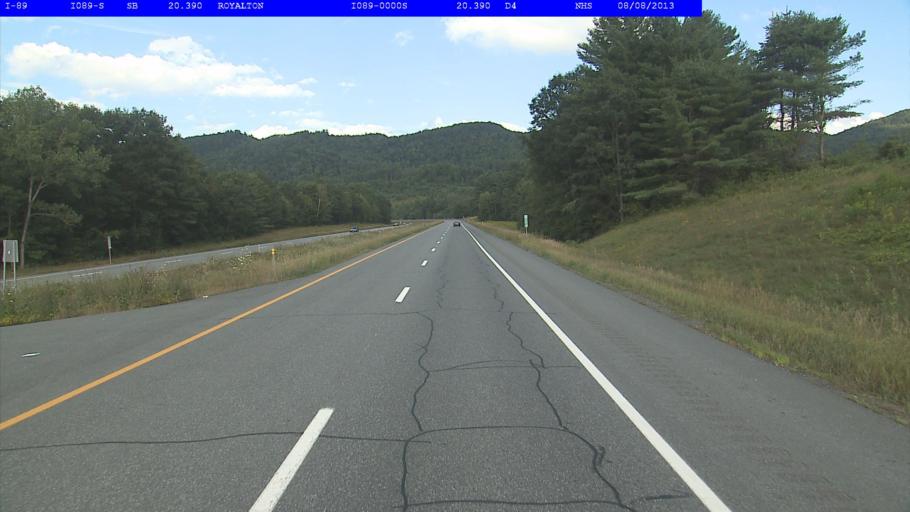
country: US
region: Vermont
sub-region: Orange County
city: Randolph
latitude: 43.8110
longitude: -72.5545
